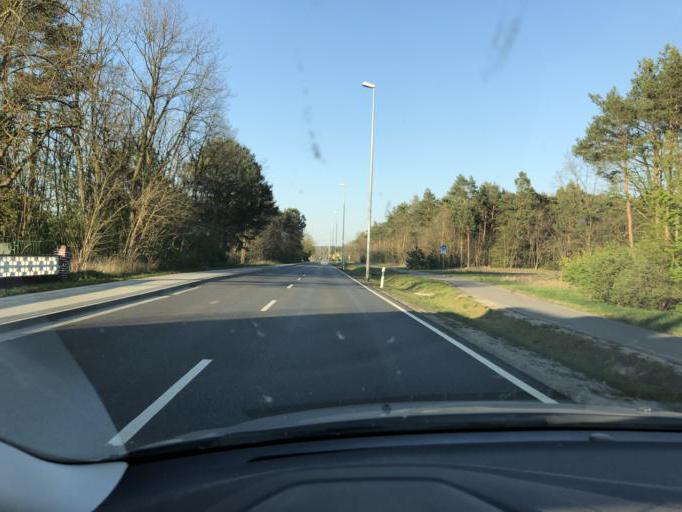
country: DE
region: Brandenburg
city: Ruhland
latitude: 51.4736
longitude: 13.8958
